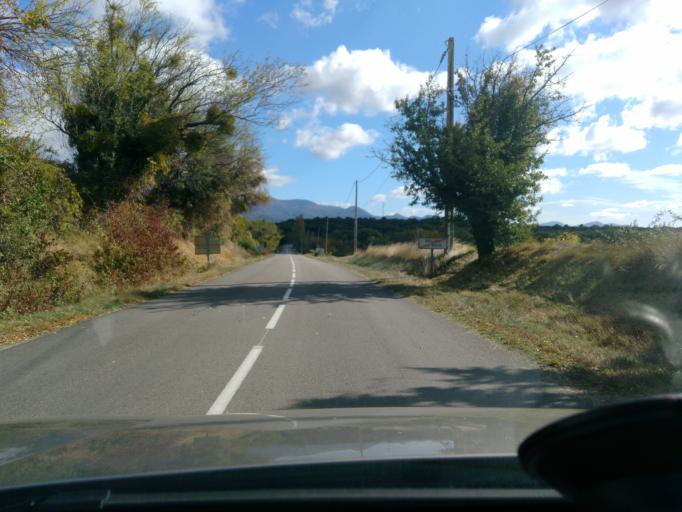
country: FR
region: Rhone-Alpes
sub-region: Departement de la Drome
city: Taulignan
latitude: 44.4507
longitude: 4.9382
